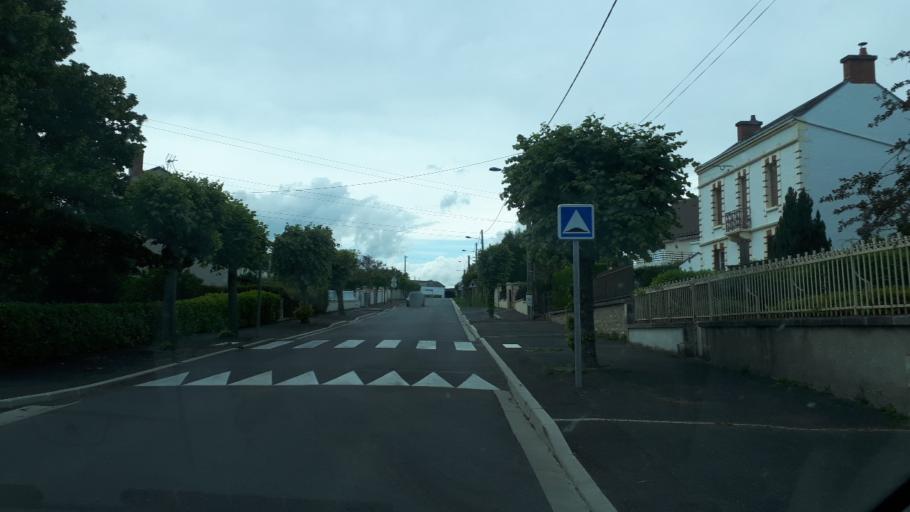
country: FR
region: Centre
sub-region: Departement de l'Indre
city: Reuilly
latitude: 47.0879
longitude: 2.0362
